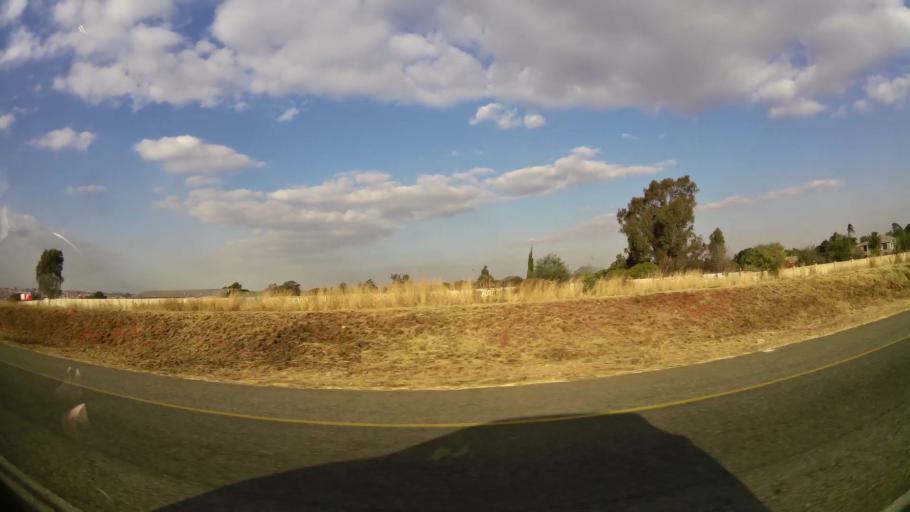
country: ZA
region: Gauteng
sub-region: West Rand District Municipality
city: Krugersdorp
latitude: -26.0881
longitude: 27.7348
